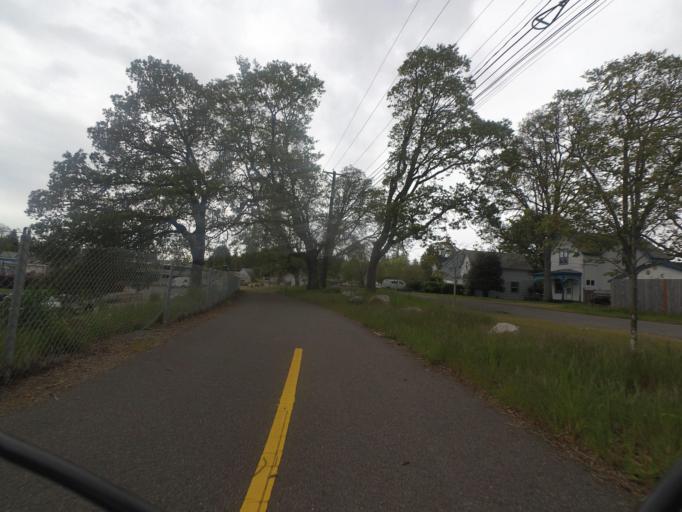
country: US
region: Washington
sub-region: Pierce County
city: Fircrest
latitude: 47.2057
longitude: -122.4778
